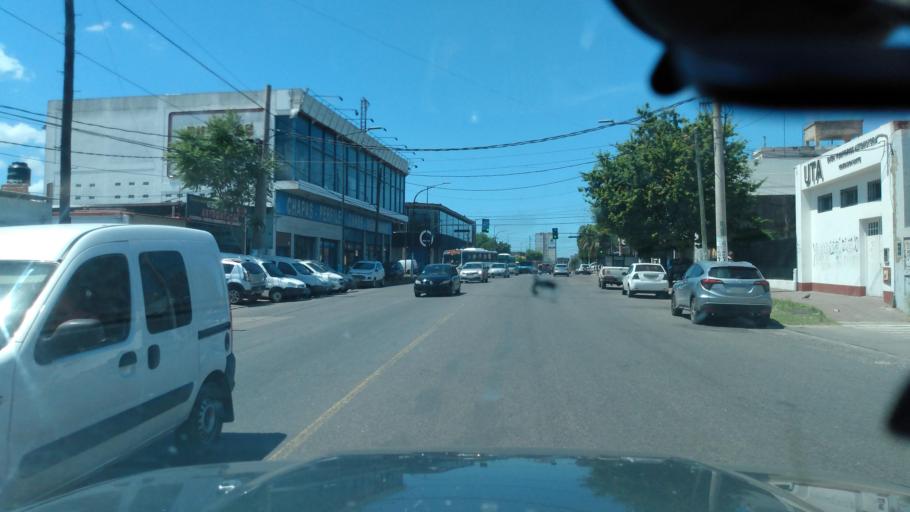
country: AR
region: Buenos Aires
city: Hurlingham
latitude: -34.5512
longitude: -58.7215
